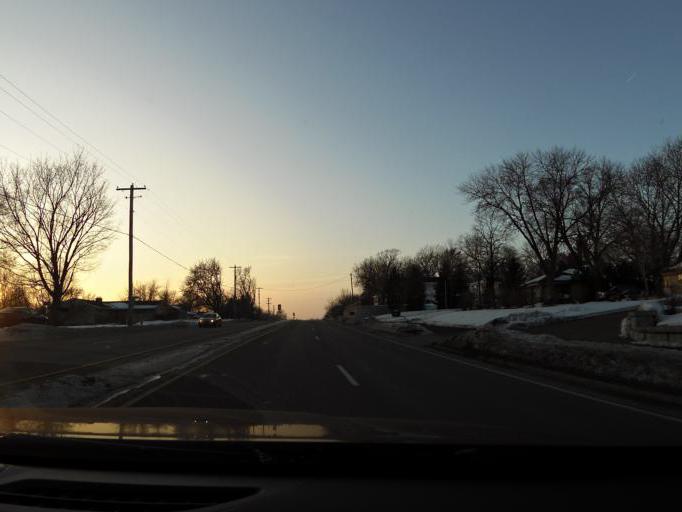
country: US
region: Minnesota
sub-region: Scott County
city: Prior Lake
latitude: 44.7178
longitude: -93.3963
